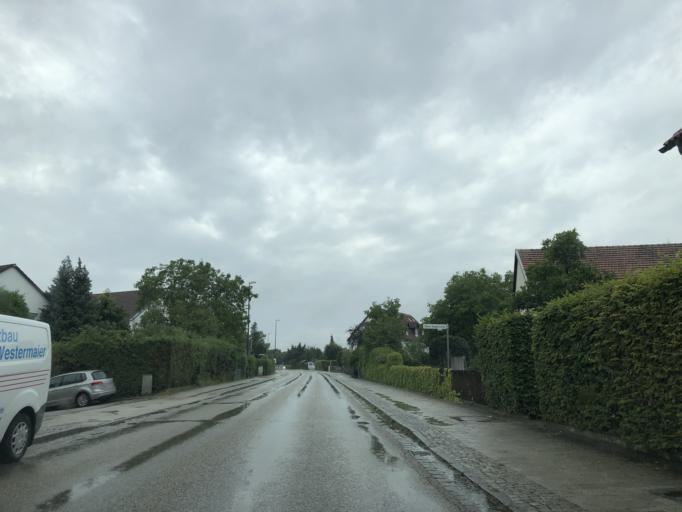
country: DE
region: Bavaria
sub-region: Upper Bavaria
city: Eching
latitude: 48.2939
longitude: 11.6184
